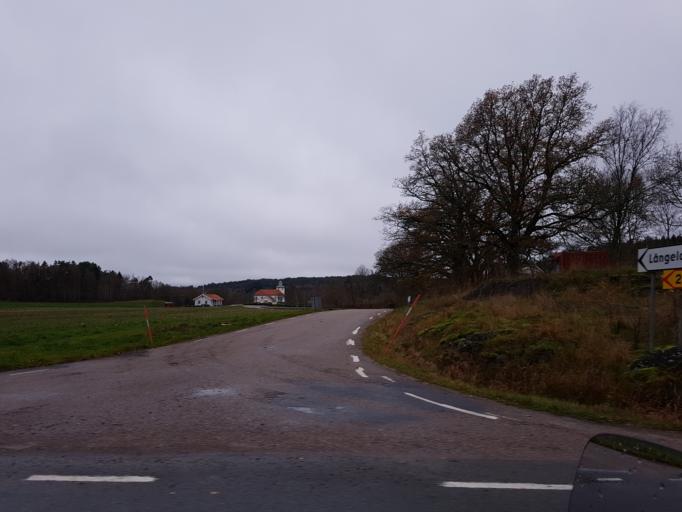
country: SE
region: Vaestra Goetaland
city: Svanesund
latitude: 58.1548
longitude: 11.7951
